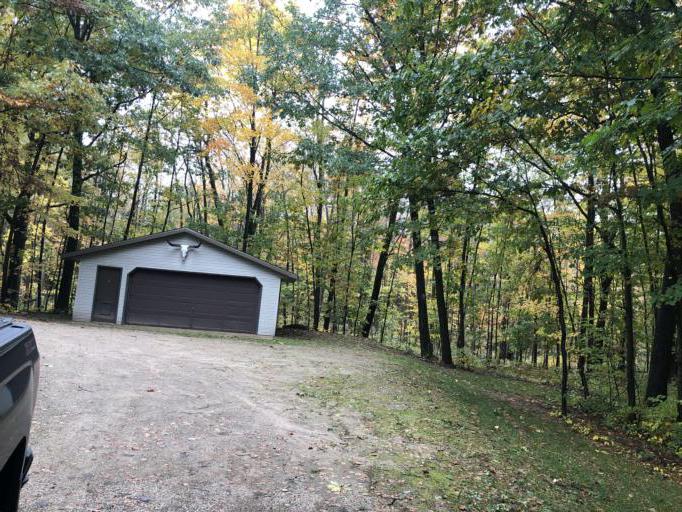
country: US
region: Wisconsin
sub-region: Oconto County
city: Oconto Falls
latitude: 44.8721
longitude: -88.0207
